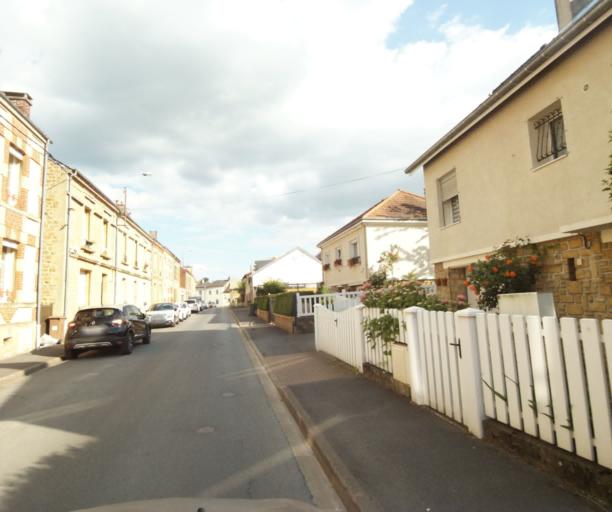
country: FR
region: Champagne-Ardenne
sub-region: Departement des Ardennes
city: Montcy-Notre-Dame
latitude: 49.7779
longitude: 4.7328
